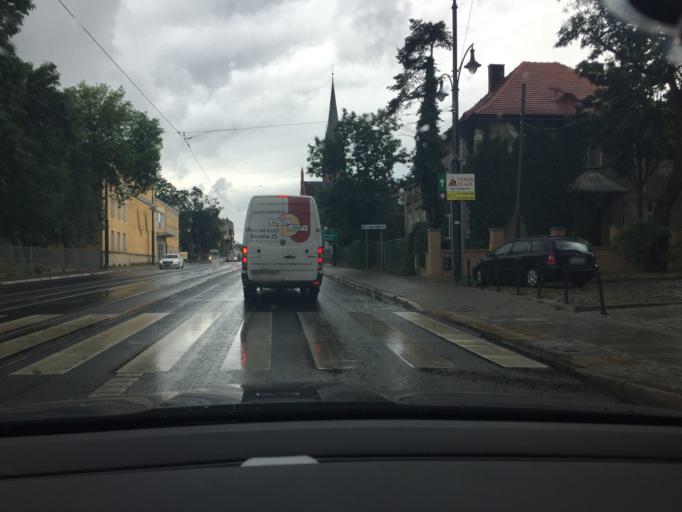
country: PL
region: Kujawsko-Pomorskie
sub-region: Torun
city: Torun
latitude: 53.0118
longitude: 18.6162
